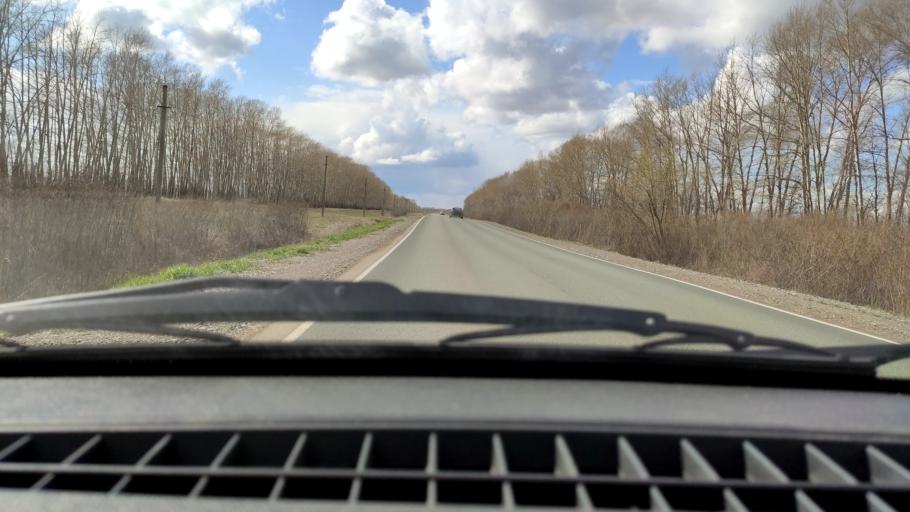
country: RU
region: Bashkortostan
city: Alekseyevka
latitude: 55.0596
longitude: 55.1089
